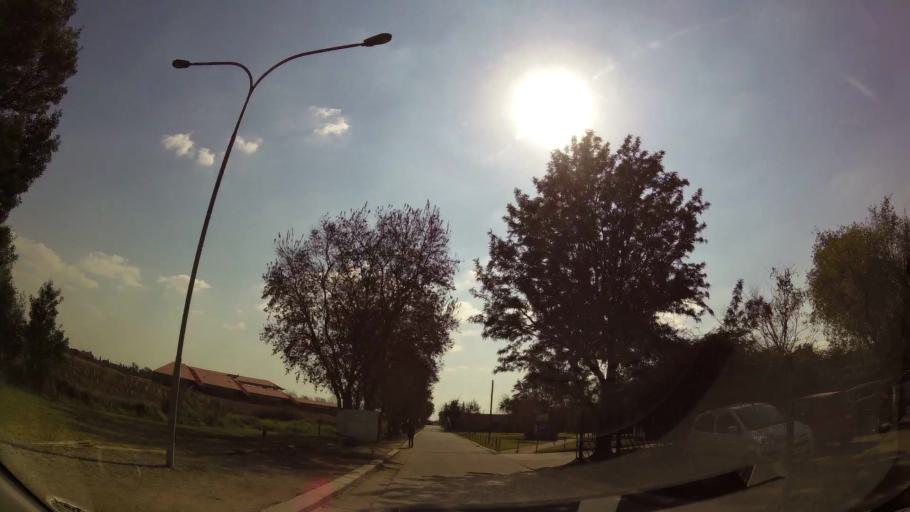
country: ZA
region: Gauteng
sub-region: Ekurhuleni Metropolitan Municipality
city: Benoni
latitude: -26.1441
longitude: 28.3975
